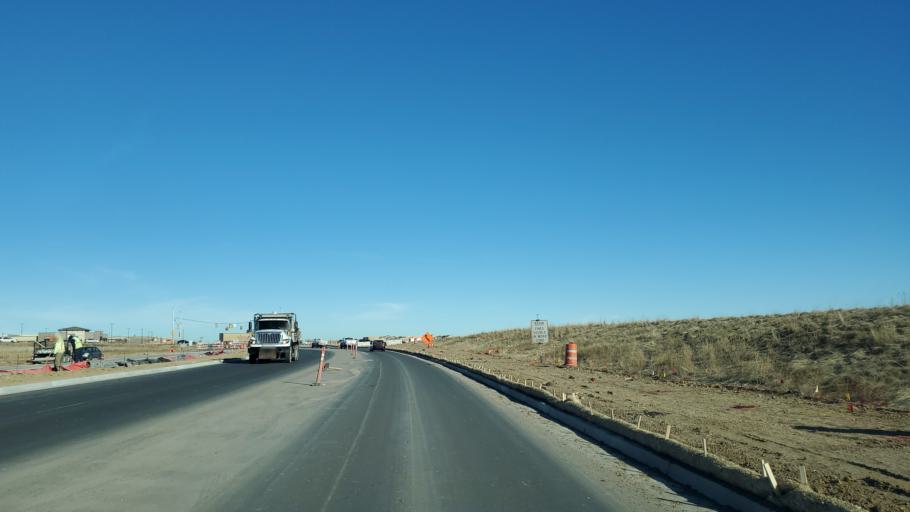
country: US
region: Colorado
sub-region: Boulder County
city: Erie
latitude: 39.9979
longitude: -105.0080
